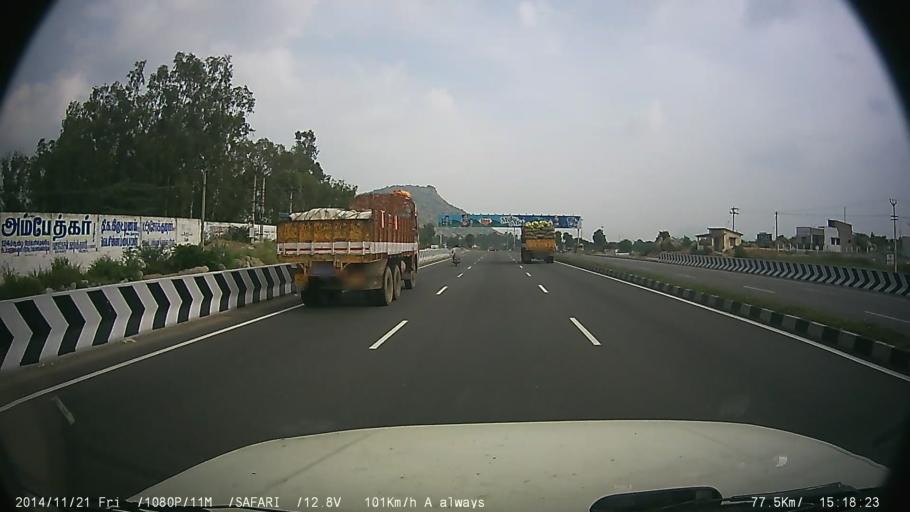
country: IN
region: Tamil Nadu
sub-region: Krishnagiri
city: Krishnagiri
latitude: 12.5479
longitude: 78.1981
